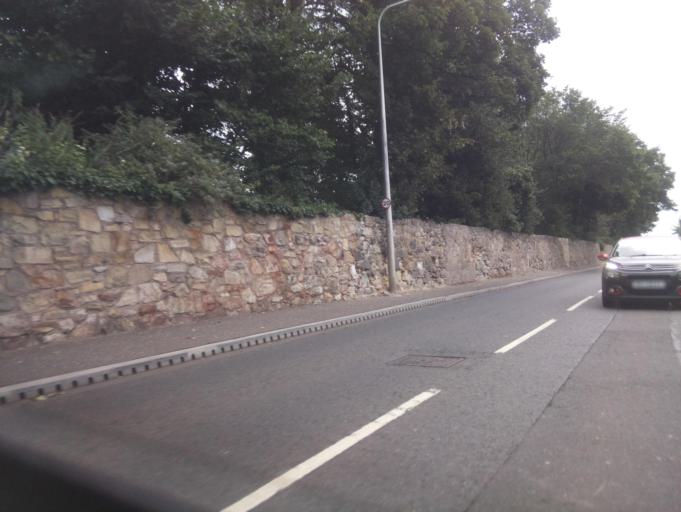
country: GB
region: Scotland
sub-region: East Lothian
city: Musselburgh
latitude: 55.9405
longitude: -3.0439
